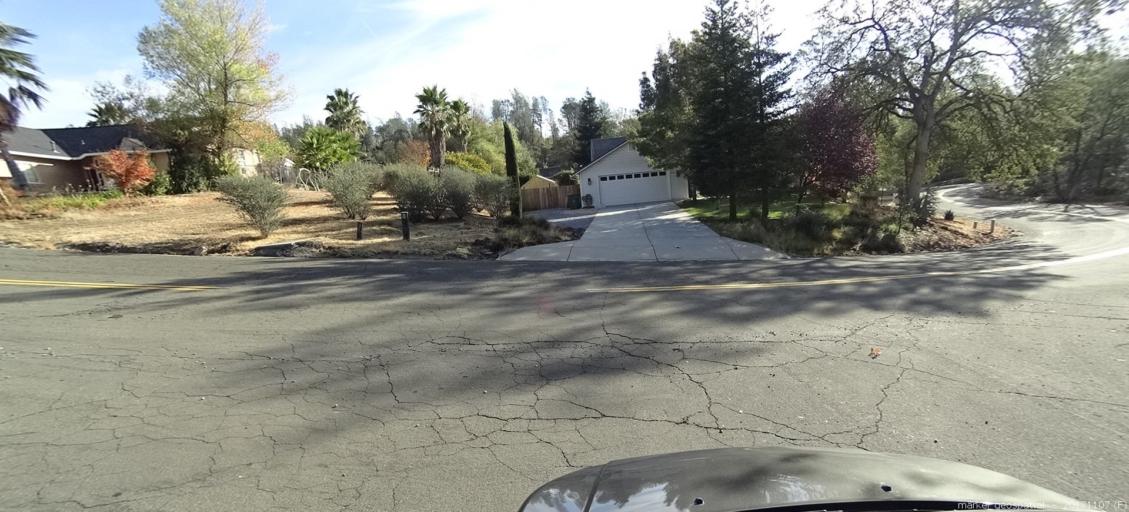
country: US
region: California
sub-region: Shasta County
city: Shasta
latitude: 40.5415
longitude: -122.4573
